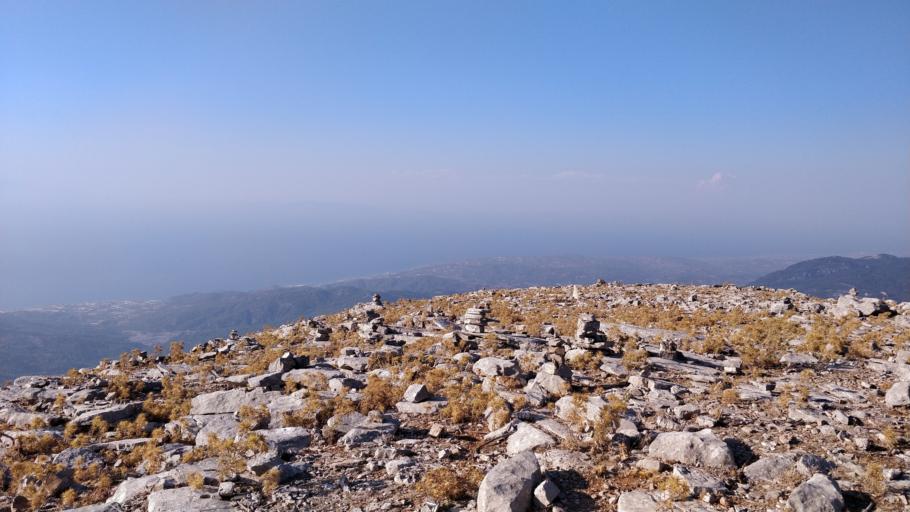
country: GR
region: South Aegean
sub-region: Nomos Dodekanisou
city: Emponas
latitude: 36.2103
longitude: 27.8636
